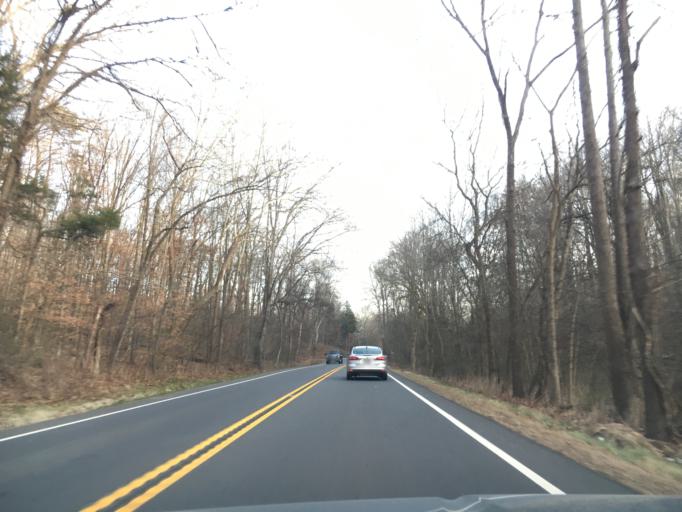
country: US
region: Virginia
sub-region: Culpeper County
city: Culpeper
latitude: 38.3479
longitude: -77.9598
